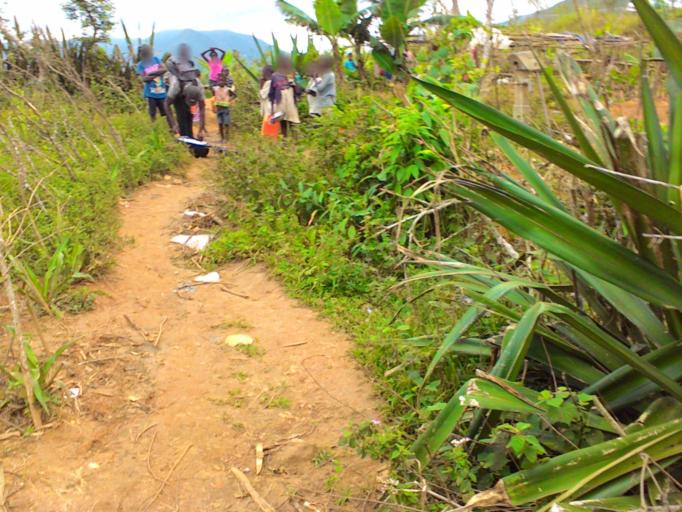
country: HT
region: Grandans
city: Moron
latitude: 18.4541
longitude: -74.1131
